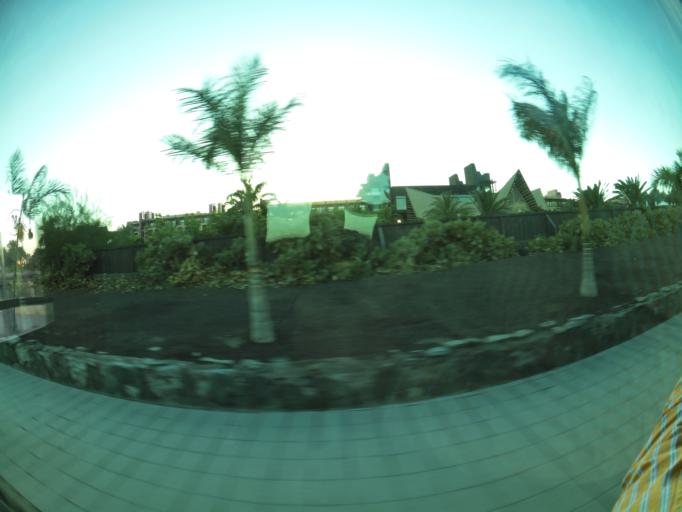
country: ES
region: Canary Islands
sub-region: Provincia de Las Palmas
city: Maspalomas
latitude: 27.7409
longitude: -15.5985
